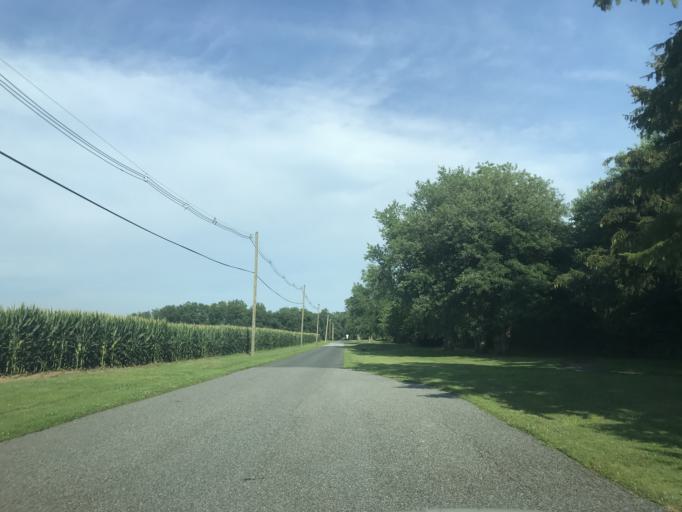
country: US
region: Maryland
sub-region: Harford County
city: Aberdeen
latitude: 39.5066
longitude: -76.1246
